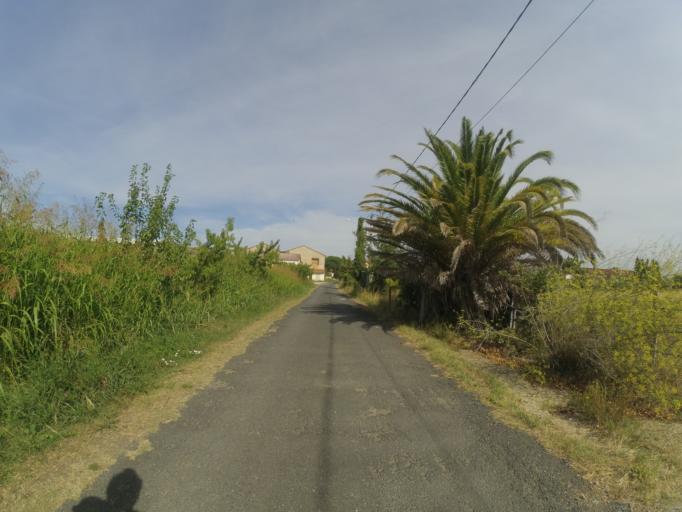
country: FR
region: Languedoc-Roussillon
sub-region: Departement des Pyrenees-Orientales
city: Ille-sur-Tet
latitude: 42.6653
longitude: 2.6232
